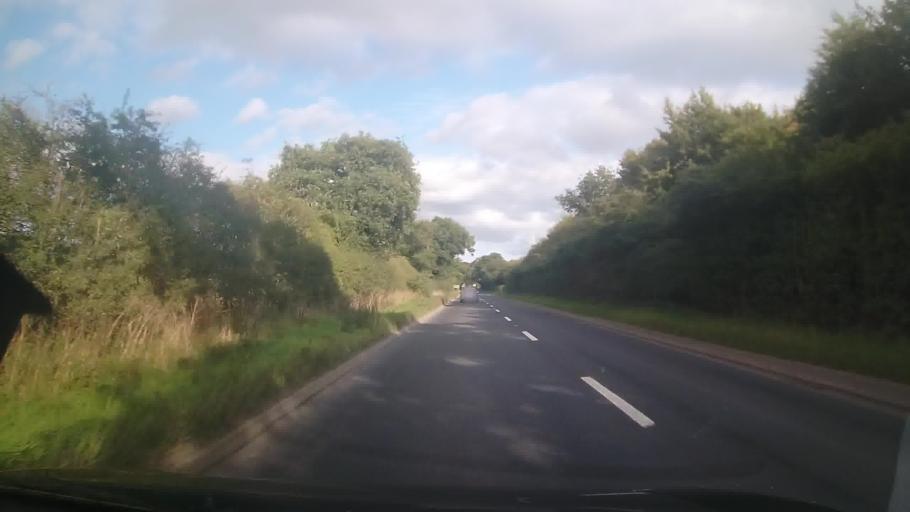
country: GB
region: England
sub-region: Shropshire
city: Bromfield
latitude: 52.3891
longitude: -2.7506
